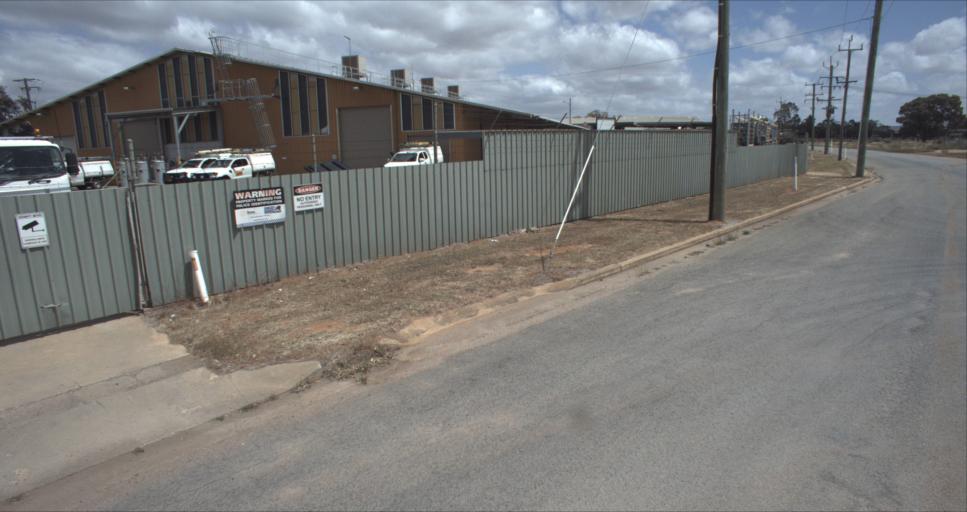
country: AU
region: New South Wales
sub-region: Leeton
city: Leeton
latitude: -34.5533
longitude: 146.3944
